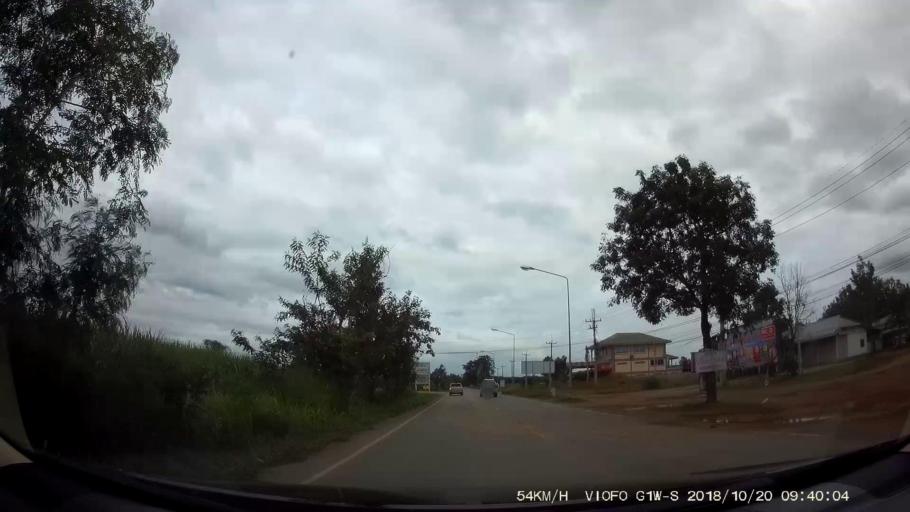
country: TH
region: Chaiyaphum
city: Kaset Sombun
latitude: 16.4398
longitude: 101.9629
